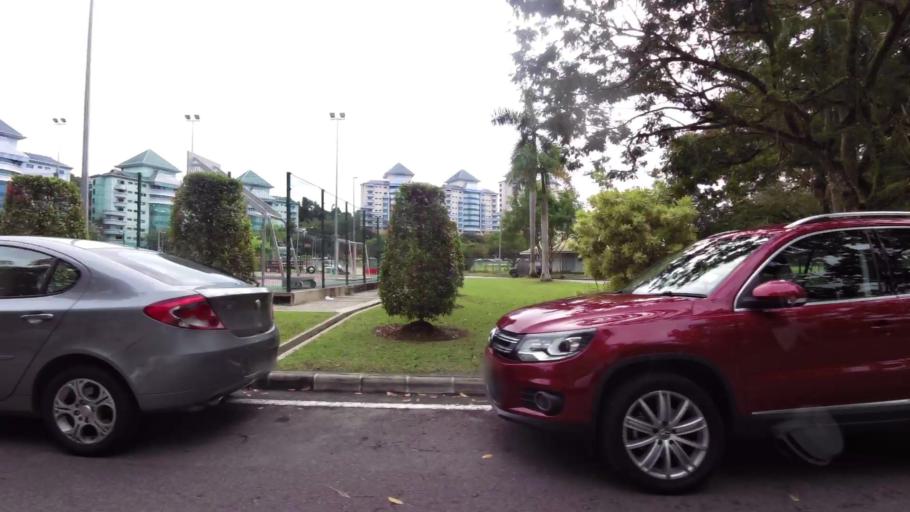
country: BN
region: Brunei and Muara
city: Bandar Seri Begawan
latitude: 4.9043
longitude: 114.9348
